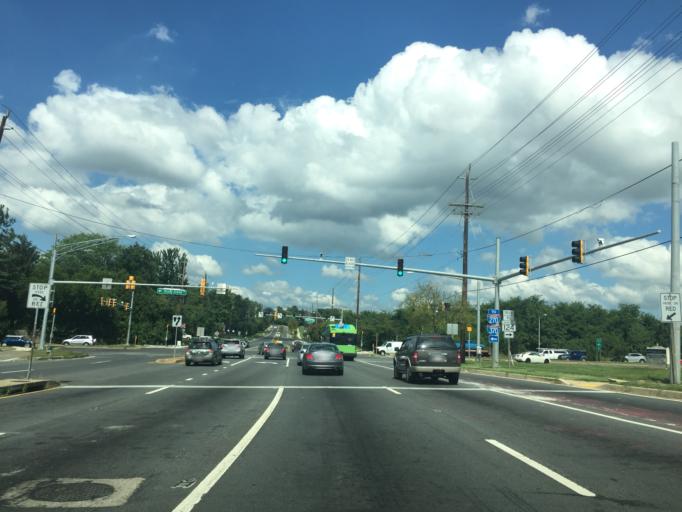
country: US
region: Maryland
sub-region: Montgomery County
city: Redland
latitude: 39.1482
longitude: -77.1463
